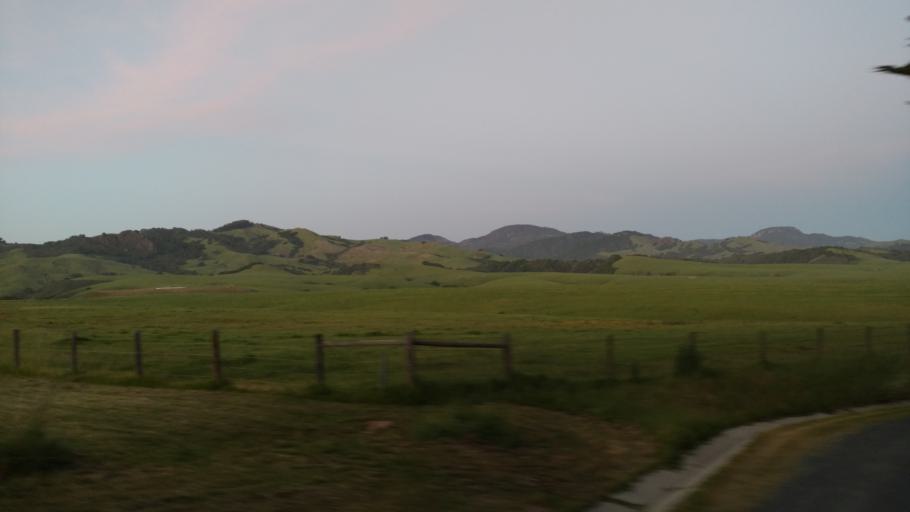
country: US
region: California
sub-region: San Luis Obispo County
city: Cambria
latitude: 35.6514
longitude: -121.1863
